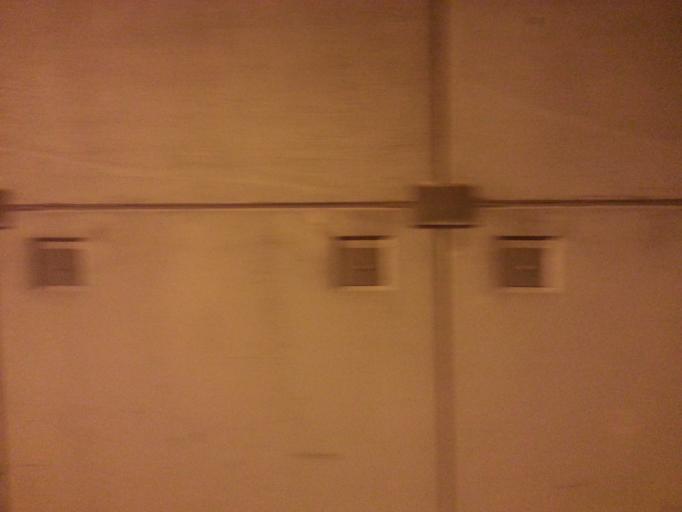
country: NO
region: Akershus
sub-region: Baerum
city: Sandvika
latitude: 59.8889
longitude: 10.5205
